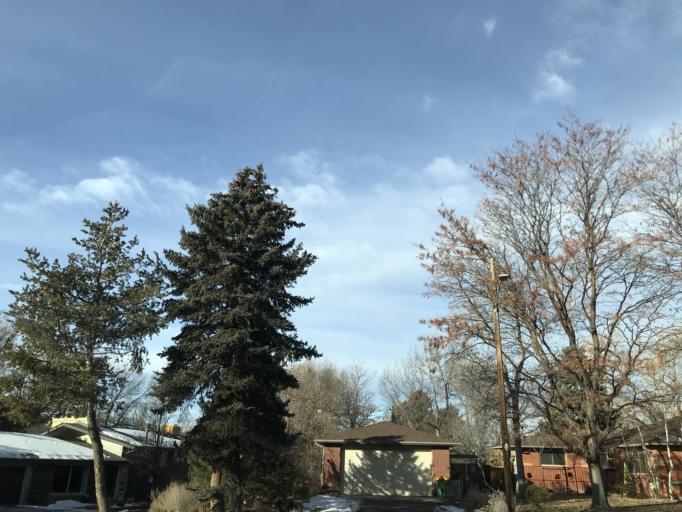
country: US
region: Colorado
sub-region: Arapahoe County
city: Littleton
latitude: 39.6097
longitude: -105.0091
